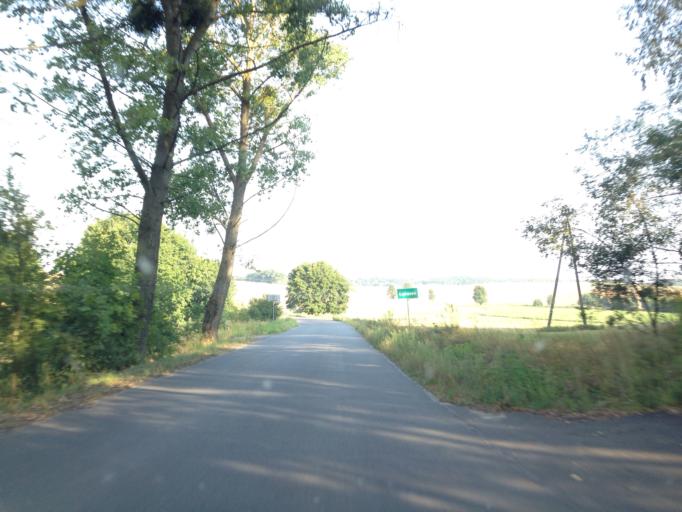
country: PL
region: Warmian-Masurian Voivodeship
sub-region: Powiat nowomiejski
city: Biskupiec
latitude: 53.4184
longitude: 19.3231
